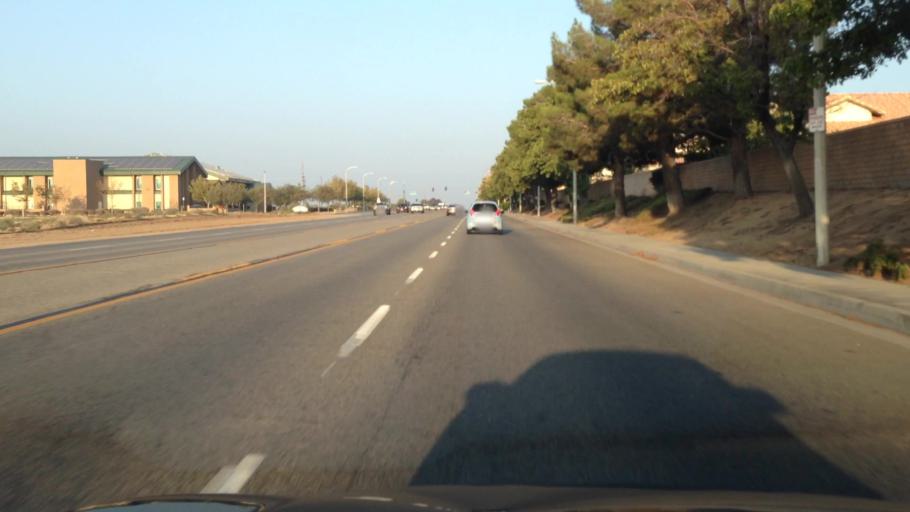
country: US
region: California
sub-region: Los Angeles County
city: Desert View Highlands
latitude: 34.6016
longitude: -118.1695
